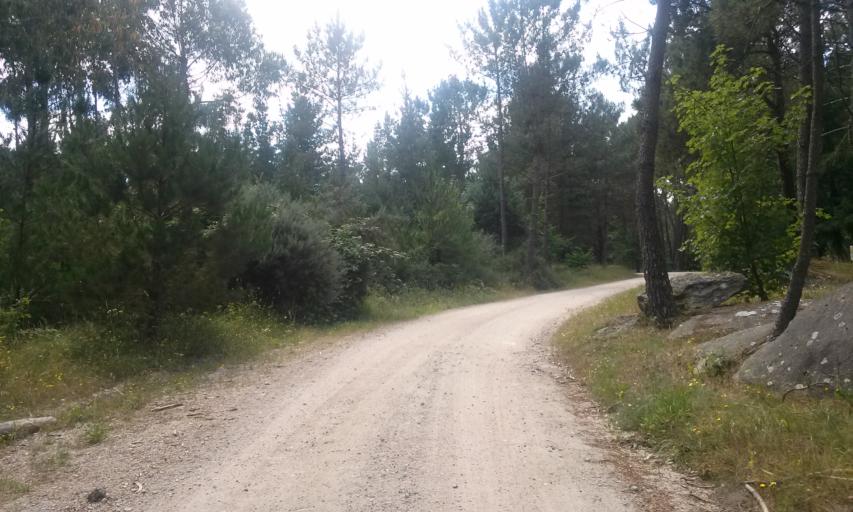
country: ES
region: Galicia
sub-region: Provincia de Lugo
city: Begonte
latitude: 43.1195
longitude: -7.6793
